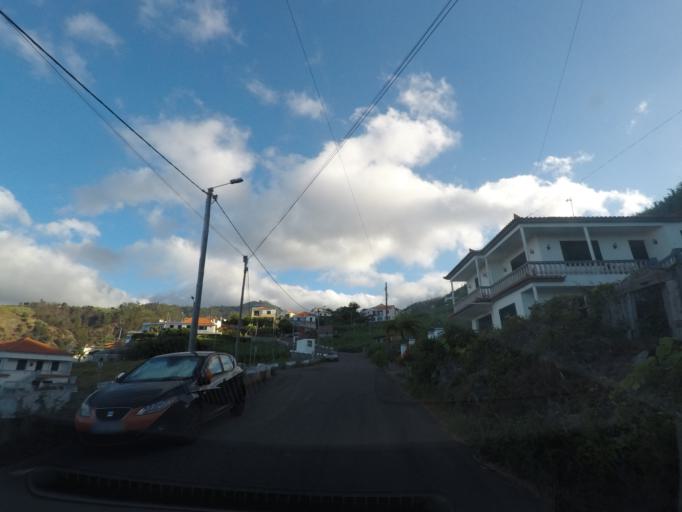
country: PT
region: Madeira
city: Ponta do Sol
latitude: 32.6934
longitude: -17.0876
